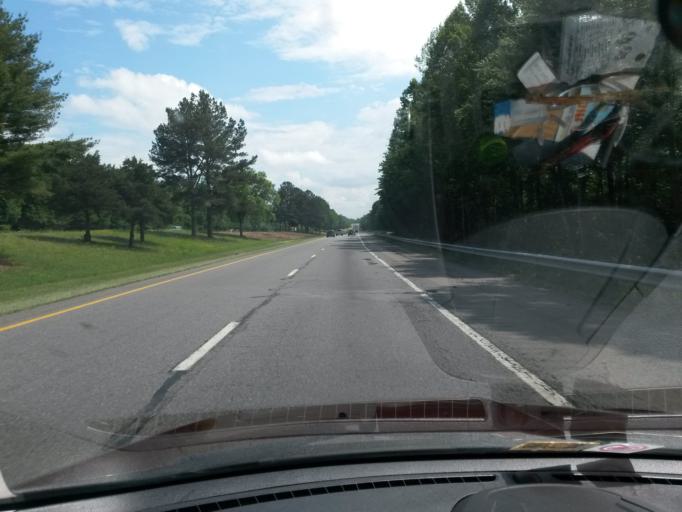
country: US
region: North Carolina
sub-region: Surry County
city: Dobson
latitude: 36.3446
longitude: -80.7952
